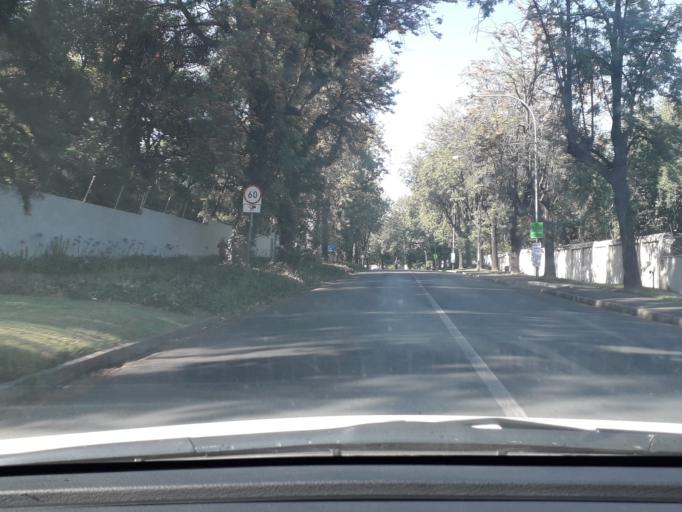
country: ZA
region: Gauteng
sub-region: City of Johannesburg Metropolitan Municipality
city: Johannesburg
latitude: -26.1560
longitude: 28.0347
